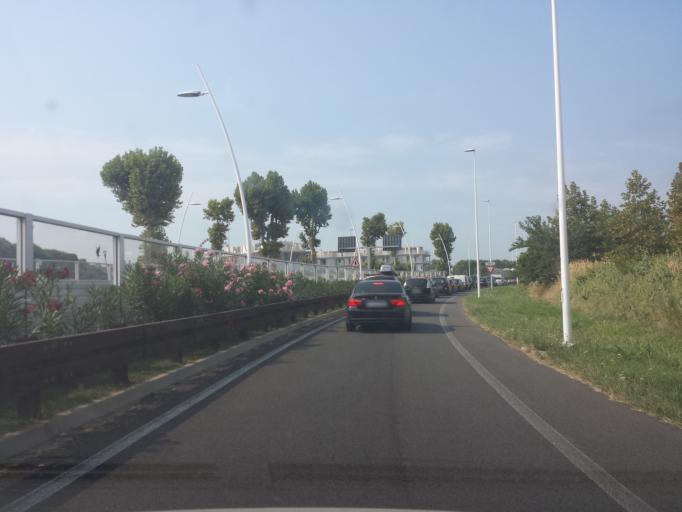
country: IT
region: Veneto
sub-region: Provincia di Venezia
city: Lido di Iesolo
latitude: 45.5083
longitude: 12.6343
